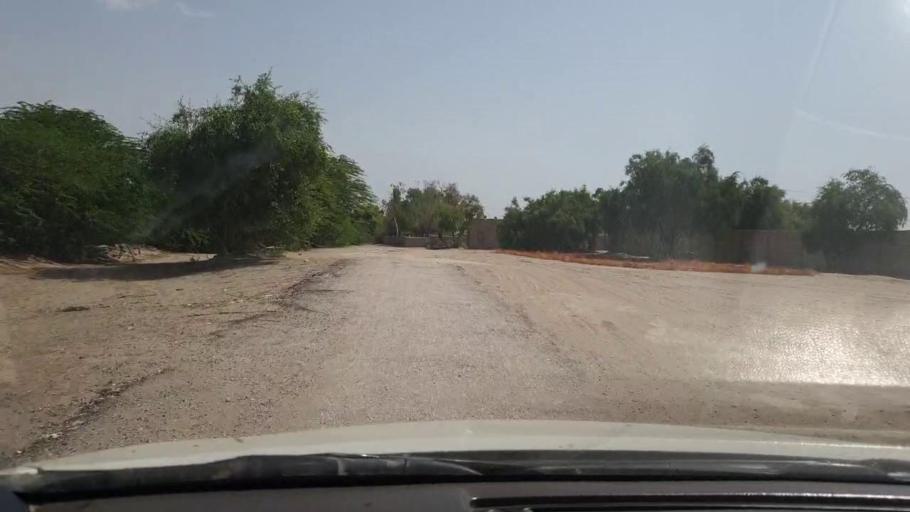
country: PK
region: Sindh
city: Rohri
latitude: 27.4642
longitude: 69.0788
